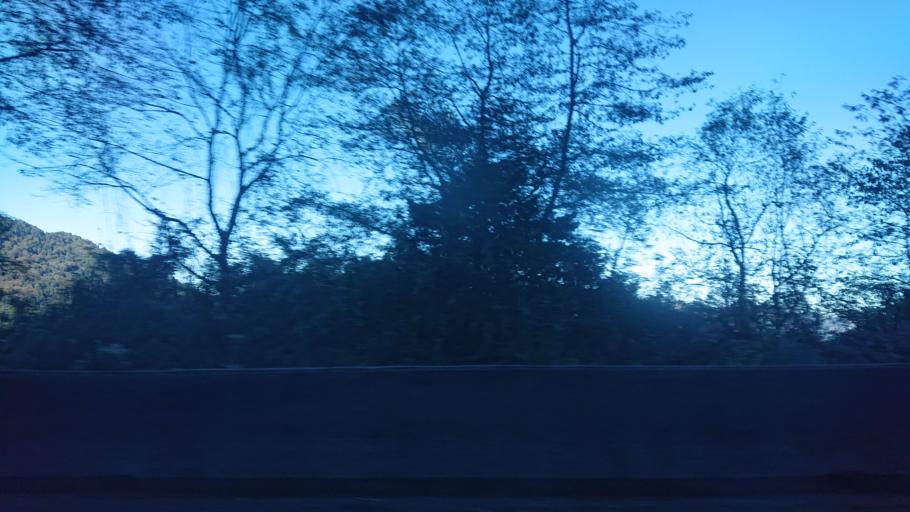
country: TW
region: Taiwan
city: Lugu
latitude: 23.4744
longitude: 120.8503
